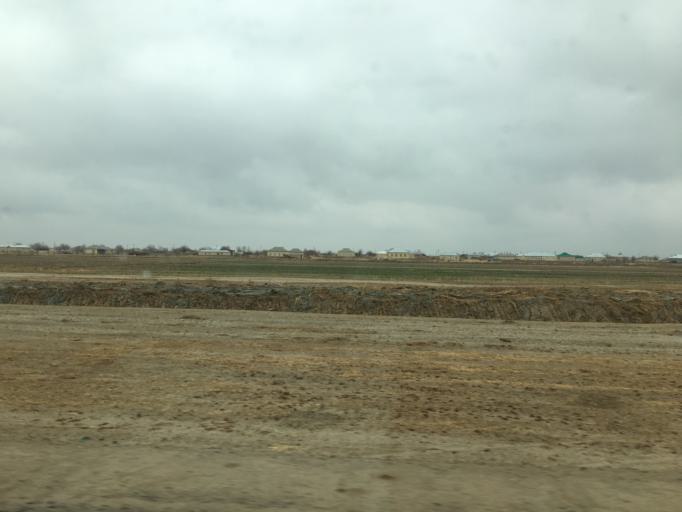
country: TM
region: Mary
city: Yoloeten
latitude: 37.3997
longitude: 62.1774
